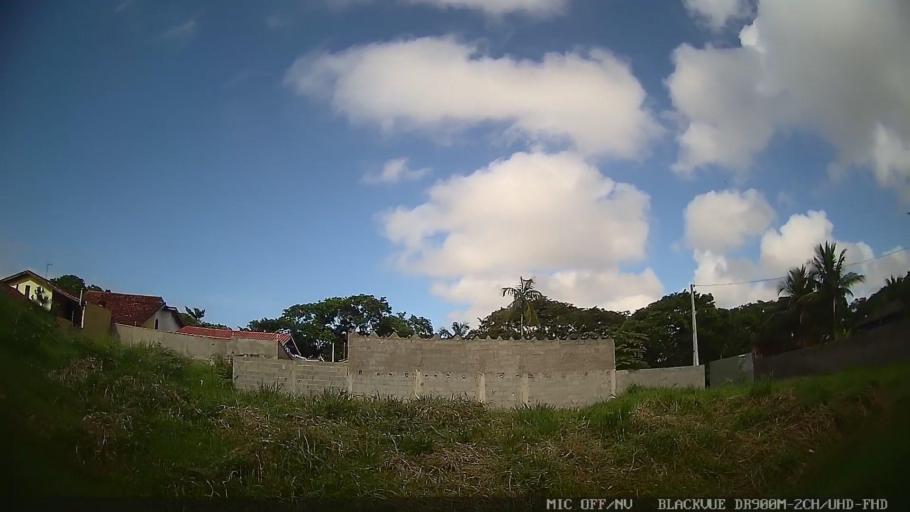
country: BR
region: Sao Paulo
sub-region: Peruibe
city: Peruibe
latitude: -24.2726
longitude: -46.9428
